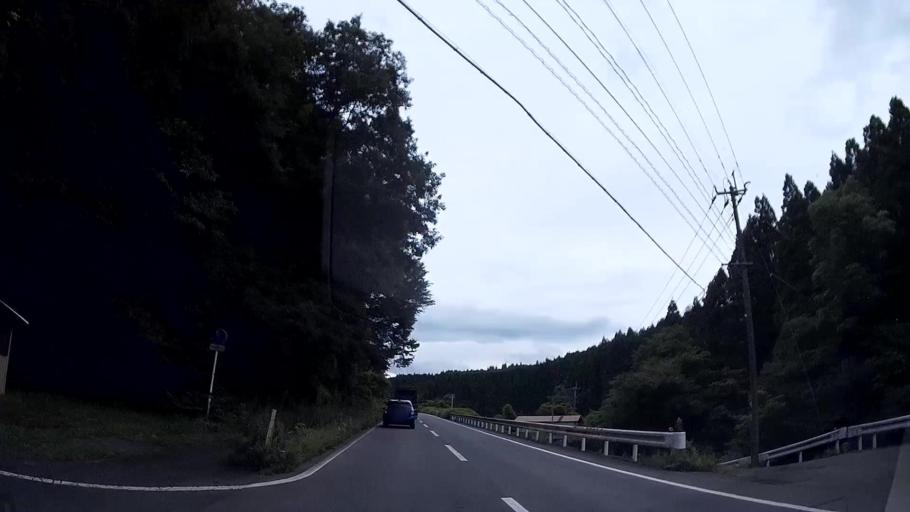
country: JP
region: Kumamoto
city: Aso
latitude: 33.1250
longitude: 131.0045
